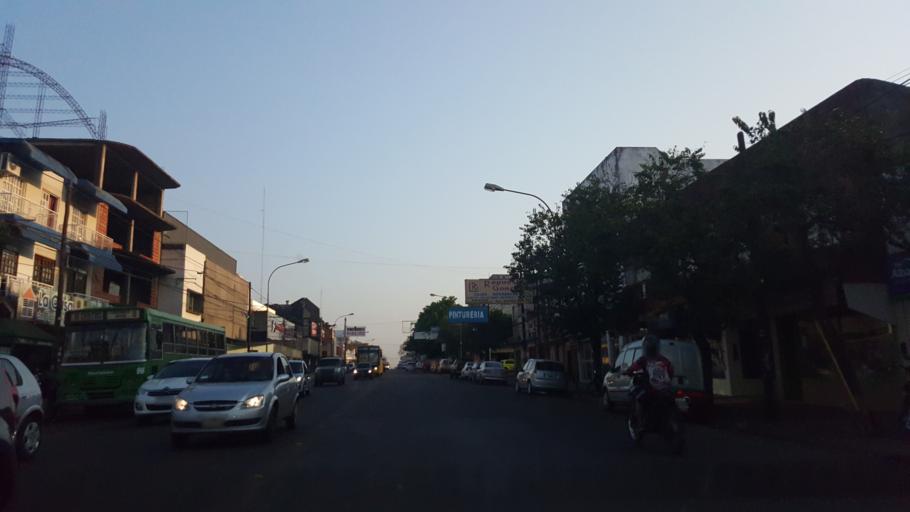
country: AR
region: Misiones
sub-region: Departamento de Capital
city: Posadas
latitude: -27.3845
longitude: -55.8999
